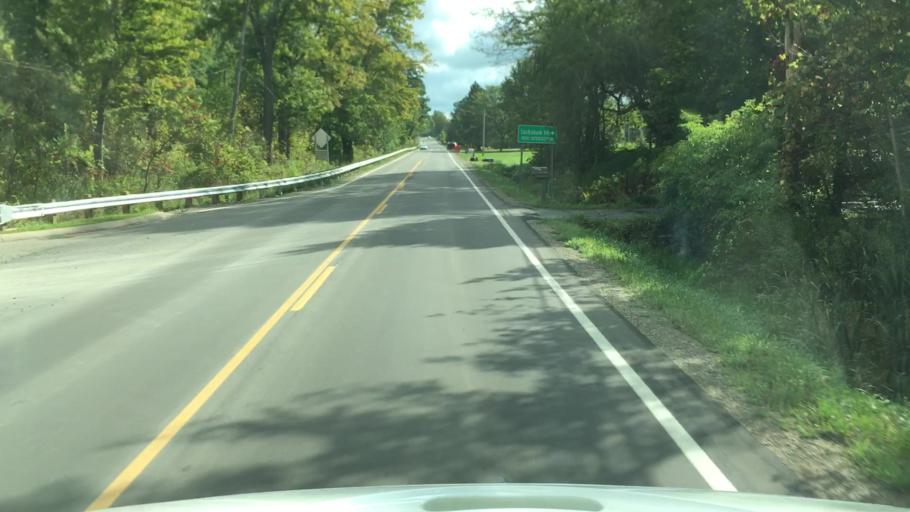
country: US
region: Michigan
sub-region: Oakland County
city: Ortonville
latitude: 42.8668
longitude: -83.3833
